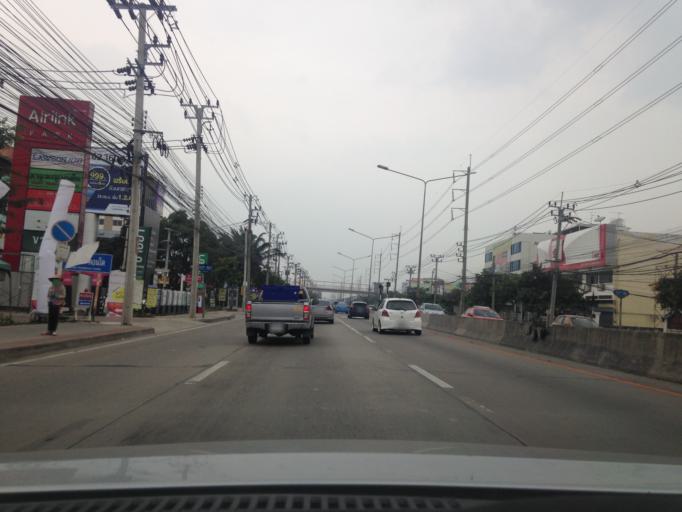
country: TH
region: Bangkok
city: Lat Krabang
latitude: 13.7360
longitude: 100.7464
